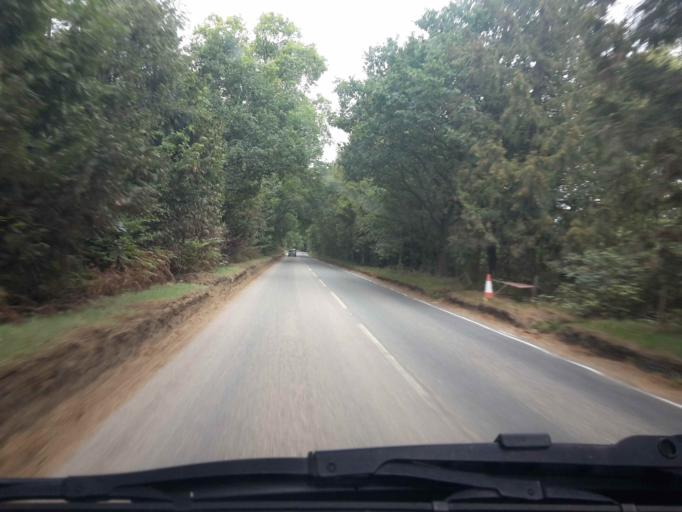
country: GB
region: England
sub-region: Hampshire
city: Eversley
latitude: 51.3309
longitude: -0.8741
